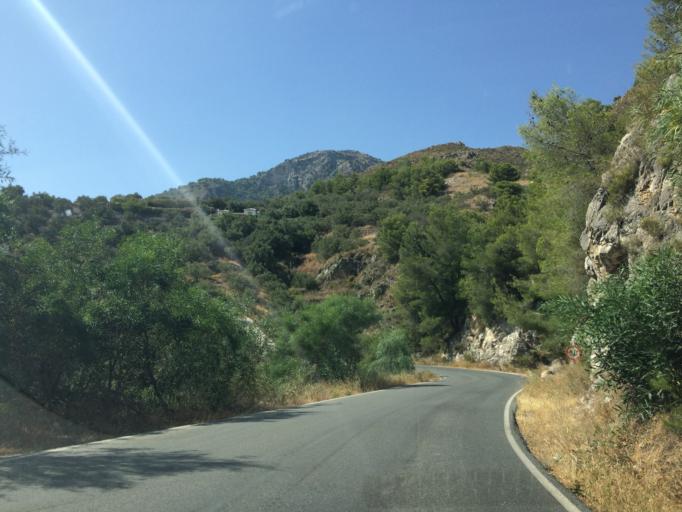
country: ES
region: Andalusia
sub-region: Provincia de Malaga
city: Frigiliana
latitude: 36.8014
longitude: -3.9086
